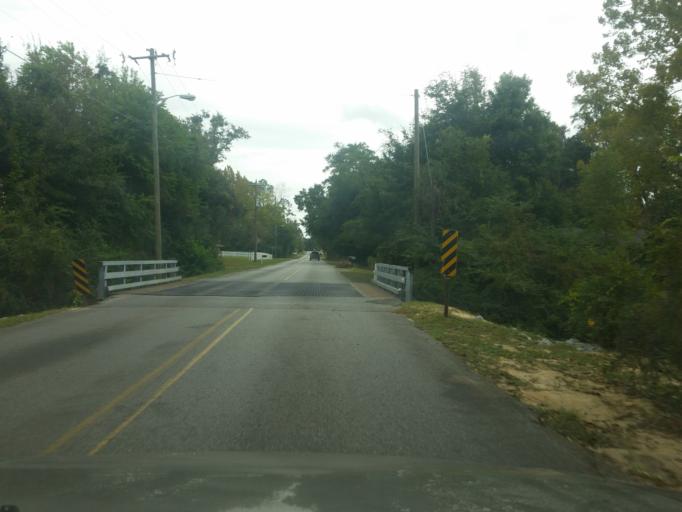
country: US
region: Florida
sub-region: Santa Rosa County
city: Milton
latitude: 30.6256
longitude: -87.0375
